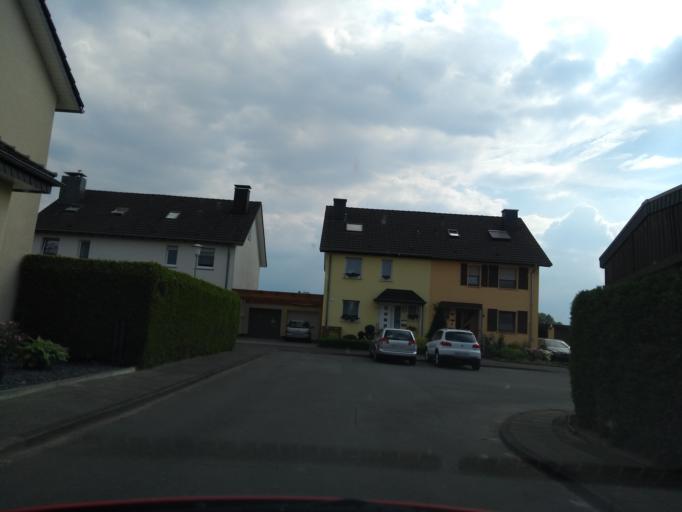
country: DE
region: North Rhine-Westphalia
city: Bad Lippspringe
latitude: 51.7640
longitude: 8.7946
